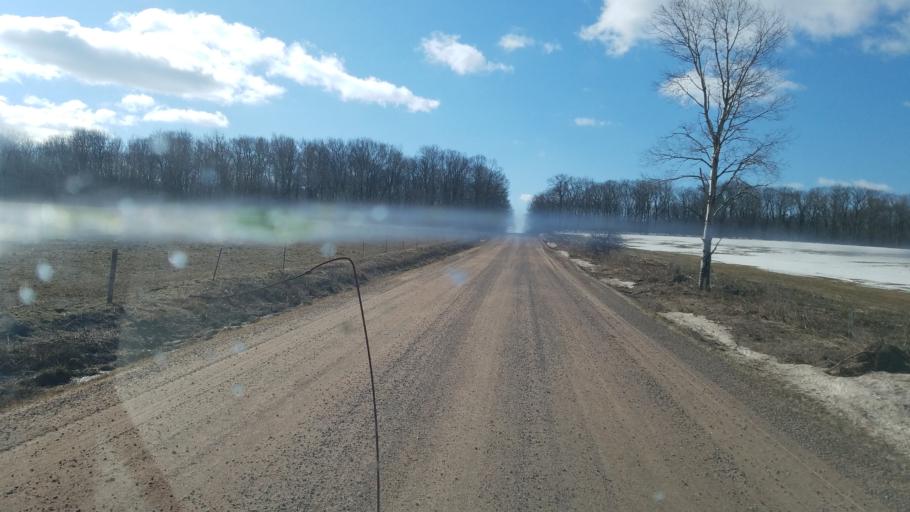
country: US
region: Wisconsin
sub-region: Clark County
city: Loyal
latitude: 44.6644
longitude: -90.4560
